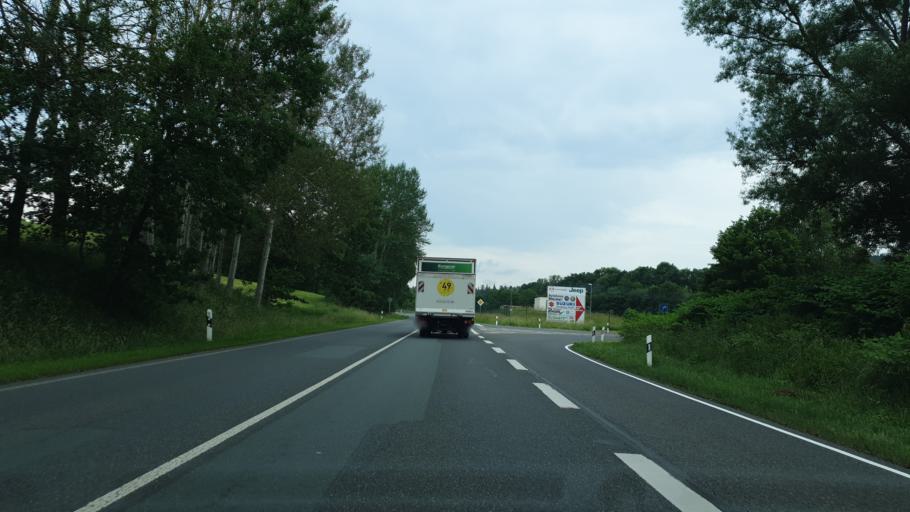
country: DE
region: Saxony
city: Rodewisch
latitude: 50.5480
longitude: 12.3875
